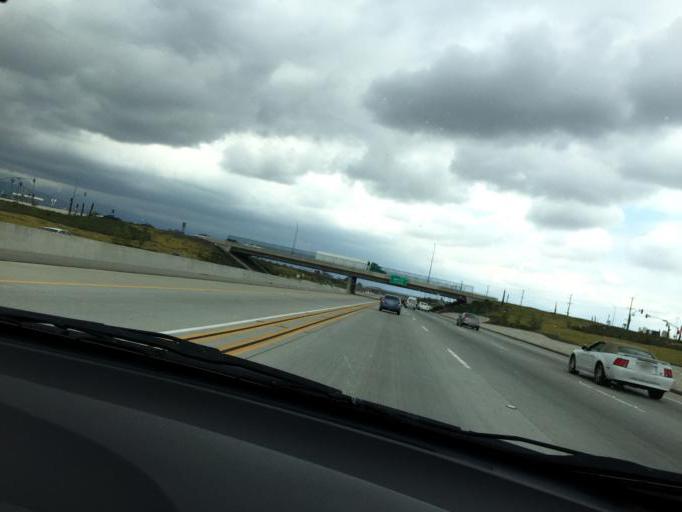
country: US
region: California
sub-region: San Bernardino County
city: Fontana
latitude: 34.1363
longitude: -117.4205
